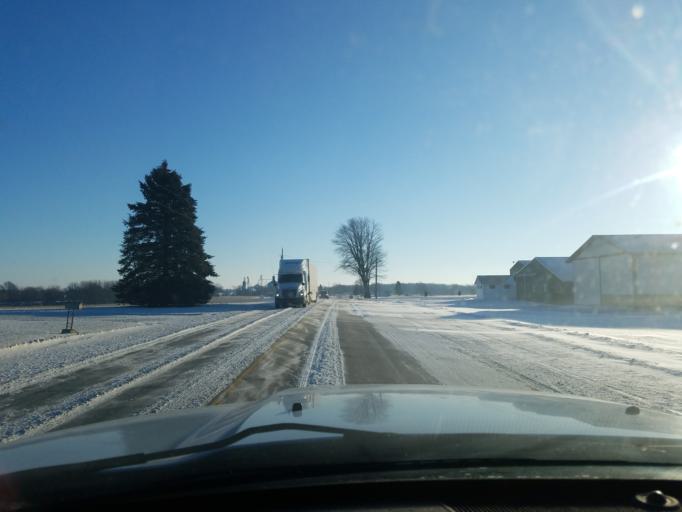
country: US
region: Indiana
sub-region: Noble County
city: Ligonier
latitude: 41.4573
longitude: -85.4973
